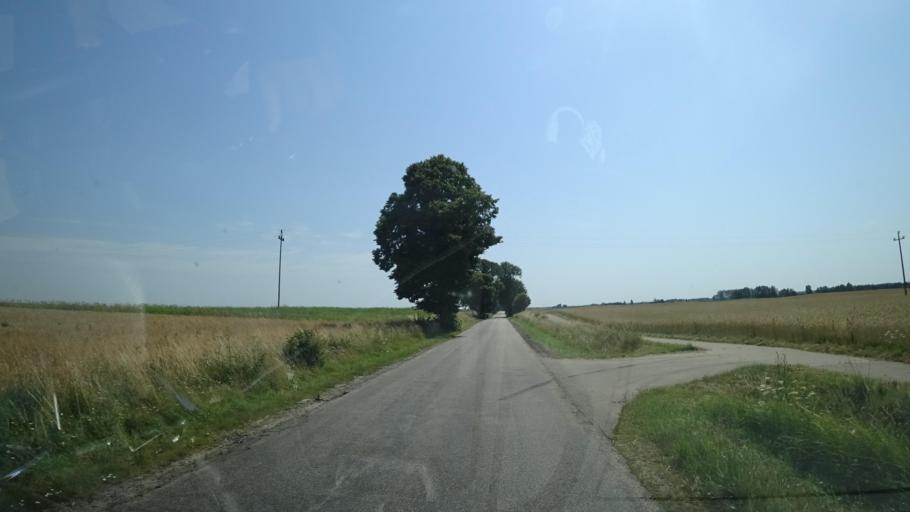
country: PL
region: Pomeranian Voivodeship
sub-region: Powiat chojnicki
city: Brusy
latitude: 53.8801
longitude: 17.6472
